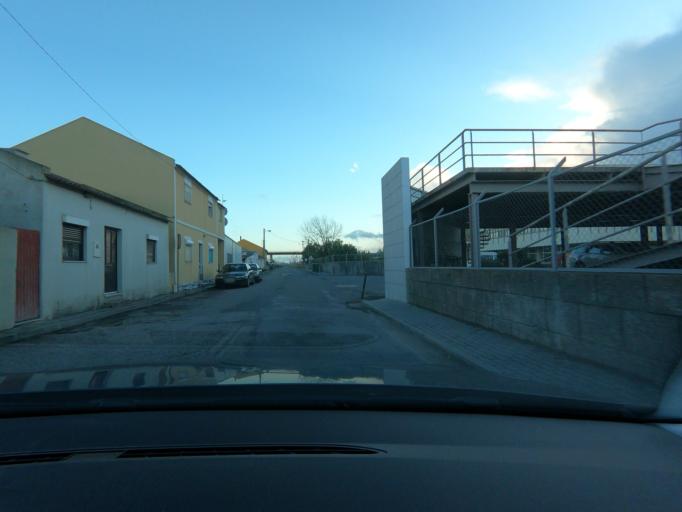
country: PT
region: Lisbon
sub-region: Vila Franca de Xira
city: Castanheira do Ribatejo
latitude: 39.0043
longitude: -8.9550
